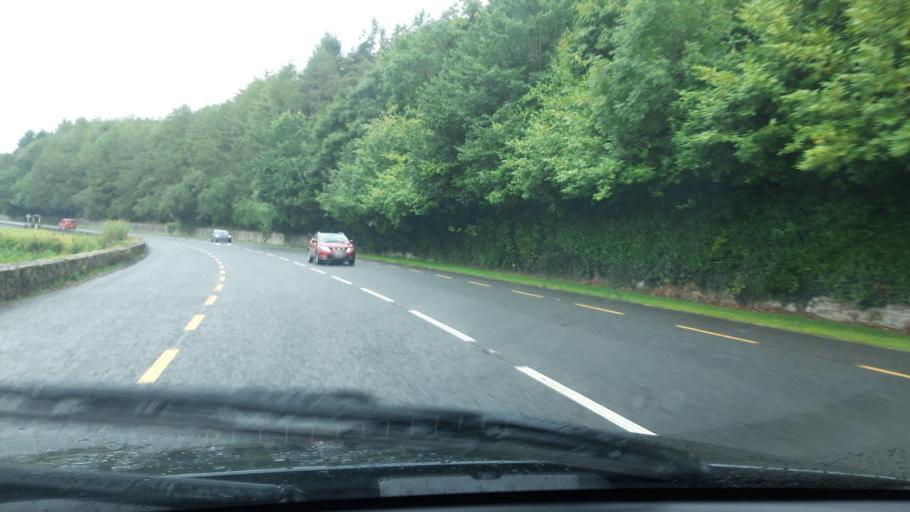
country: IE
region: Munster
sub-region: County Cork
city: Youghal
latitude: 52.1502
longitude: -7.8740
